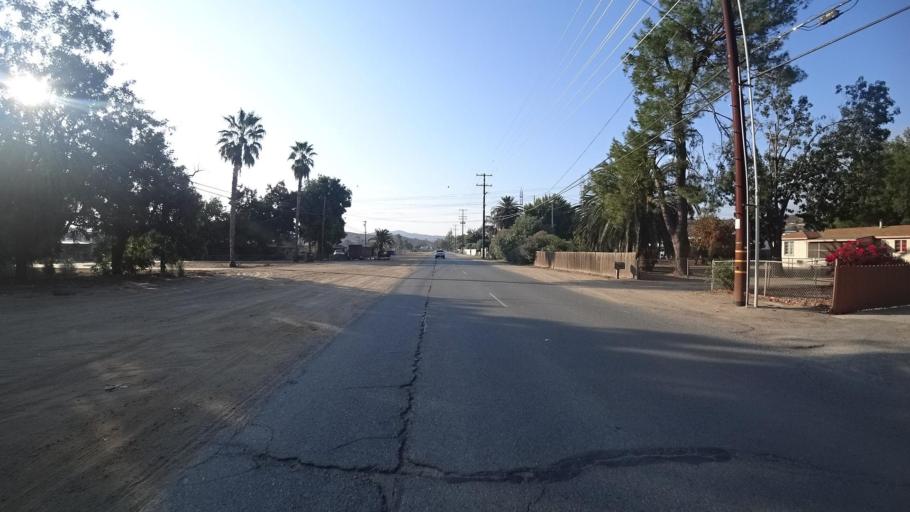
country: US
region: California
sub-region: San Diego County
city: Lakeside
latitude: 32.8802
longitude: -116.9227
